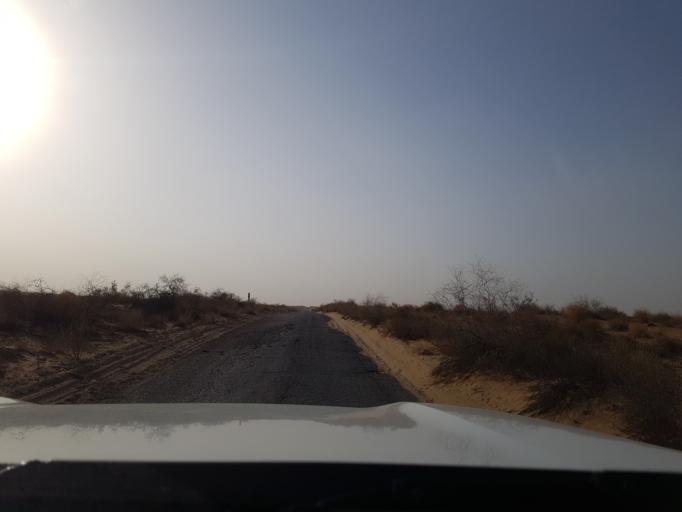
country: UZ
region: Xorazm
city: Hazorasp
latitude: 41.1978
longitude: 60.9463
